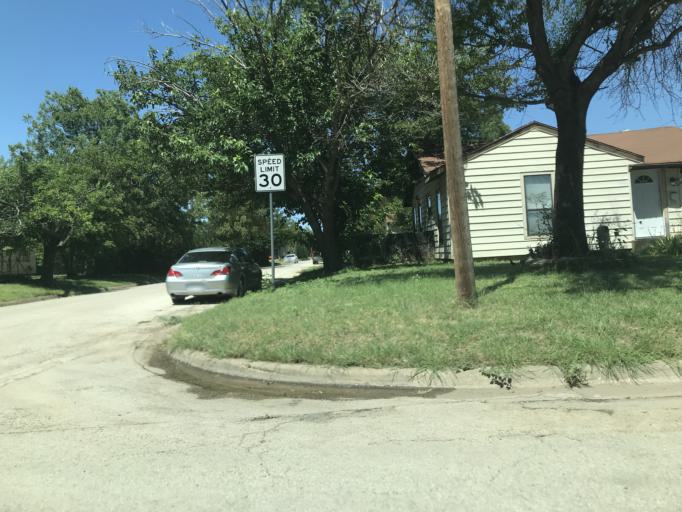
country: US
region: Texas
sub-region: Taylor County
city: Abilene
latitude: 32.4227
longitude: -99.7449
